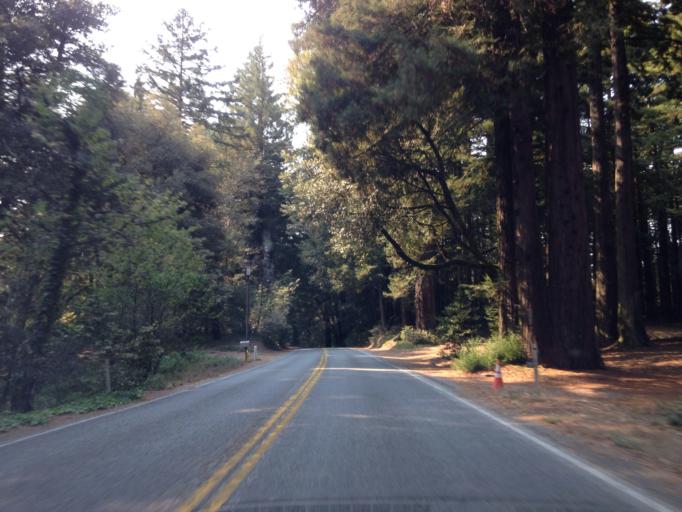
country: US
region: California
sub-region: San Mateo County
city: Emerald Lake Hills
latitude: 37.4463
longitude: -122.3309
